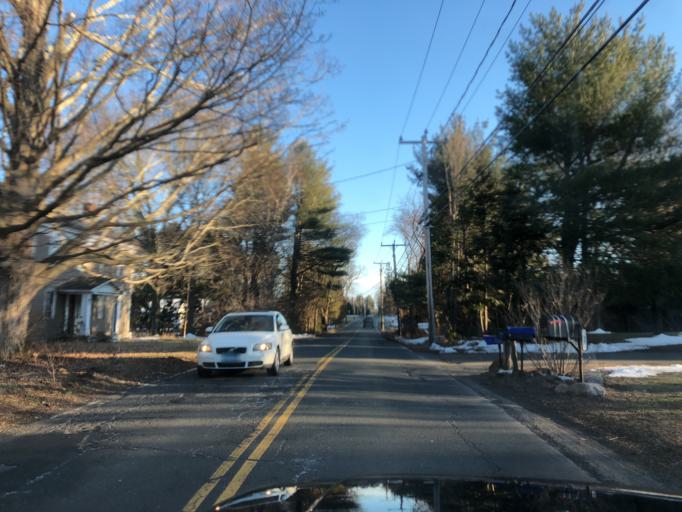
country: US
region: Connecticut
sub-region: Hartford County
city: Farmington
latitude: 41.7681
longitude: -72.8593
